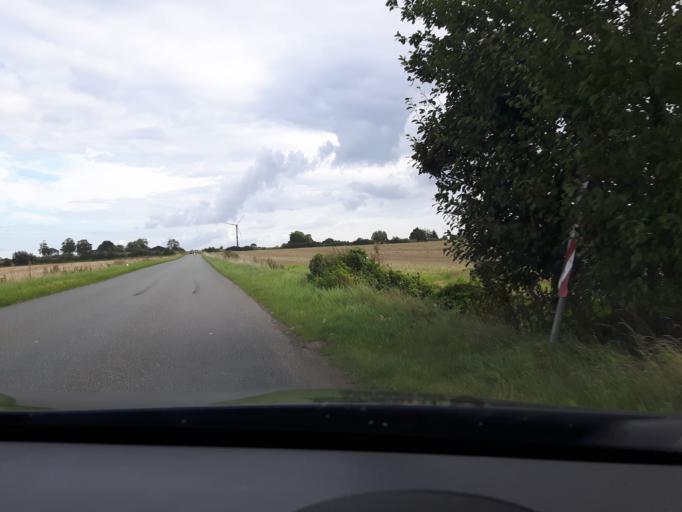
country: DK
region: South Denmark
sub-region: Fredericia Kommune
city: Fredericia
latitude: 55.6087
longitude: 9.7604
